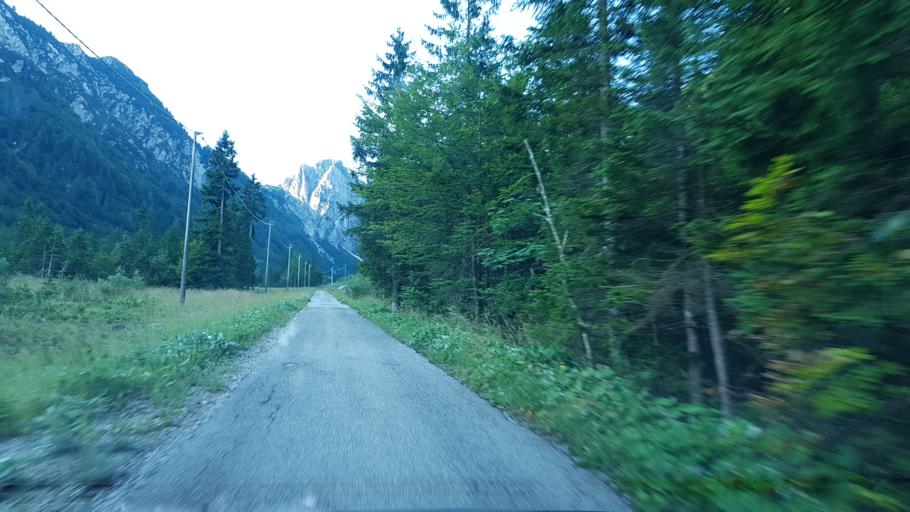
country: IT
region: Friuli Venezia Giulia
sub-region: Provincia di Udine
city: Pontebba
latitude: 46.4979
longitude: 13.2535
